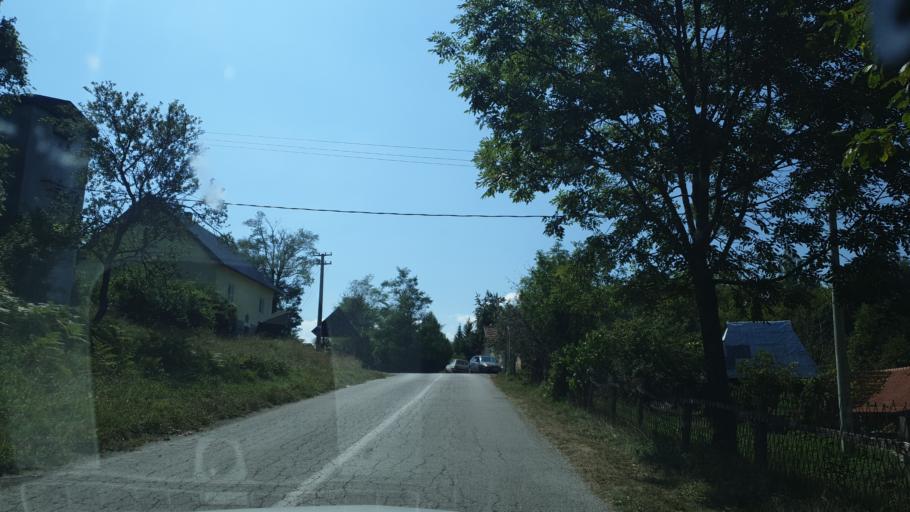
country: RS
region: Central Serbia
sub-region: Zlatiborski Okrug
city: Cajetina
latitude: 43.6920
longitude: 19.8480
